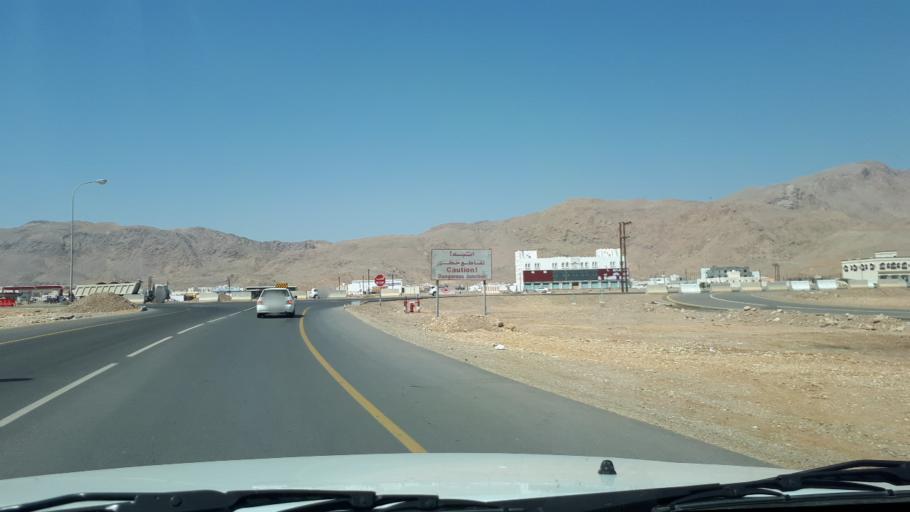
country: OM
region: Ash Sharqiyah
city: Sur
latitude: 22.5972
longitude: 59.4364
